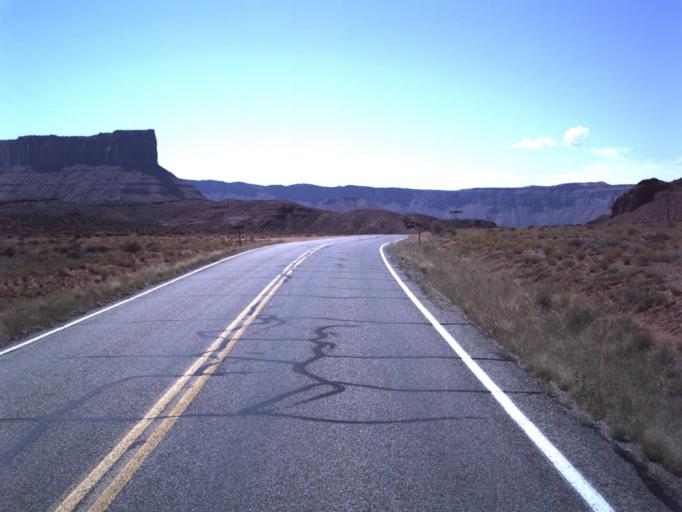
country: US
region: Utah
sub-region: Grand County
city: Moab
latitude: 38.7081
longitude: -109.3798
